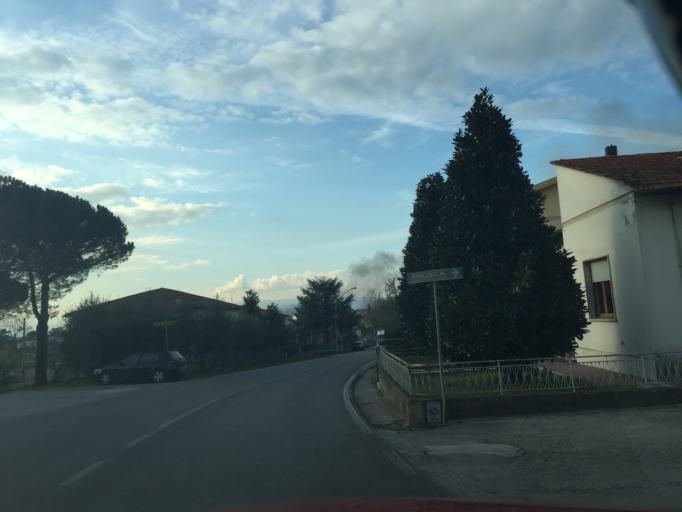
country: IT
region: Tuscany
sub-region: Provincia di Pistoia
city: San Rocco
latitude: 43.8246
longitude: 10.8678
